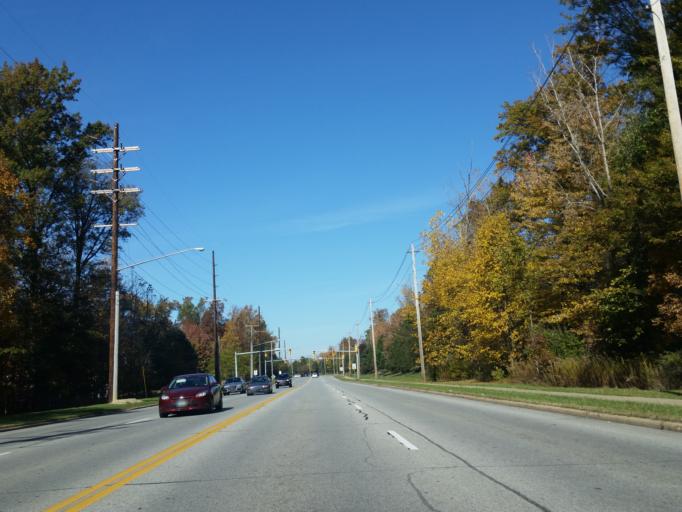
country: US
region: Ohio
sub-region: Cuyahoga County
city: Westlake
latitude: 41.4408
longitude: -81.9474
